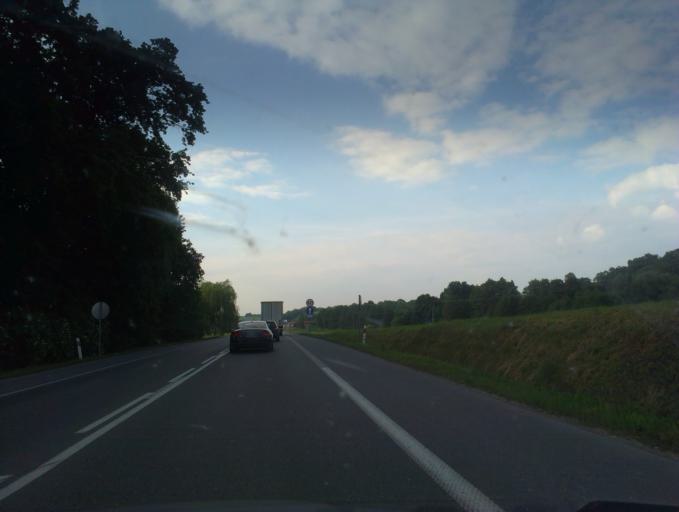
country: PL
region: Lower Silesian Voivodeship
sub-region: Powiat trzebnicki
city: Trzebnica
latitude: 51.2813
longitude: 17.0470
